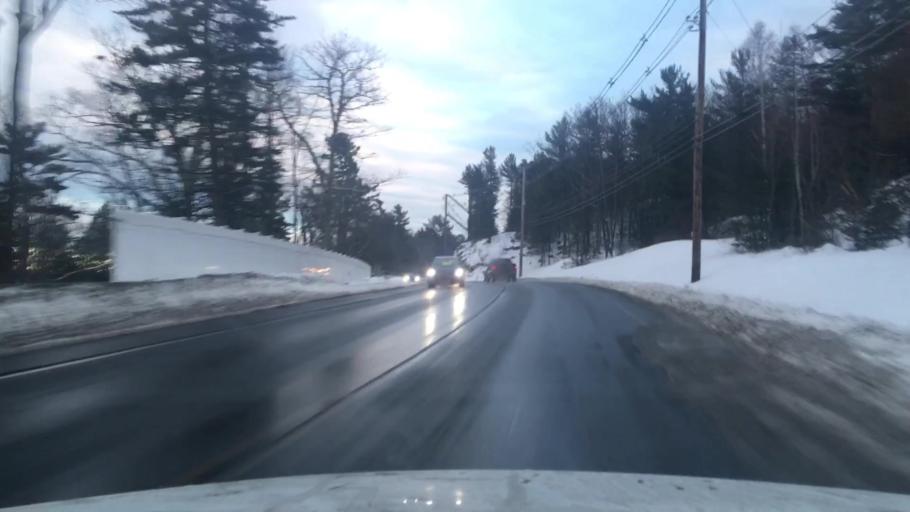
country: US
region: Maine
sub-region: Hancock County
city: Bar Harbor
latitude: 44.4048
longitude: -68.2347
